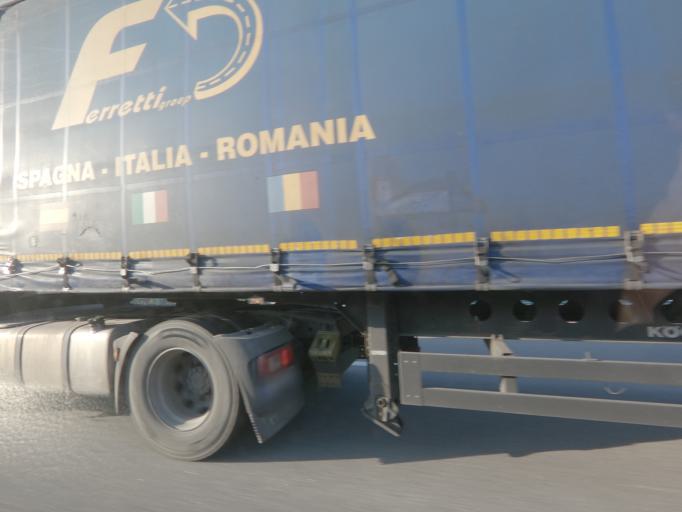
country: PT
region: Porto
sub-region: Amarante
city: Amarante
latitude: 41.2616
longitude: -8.0282
